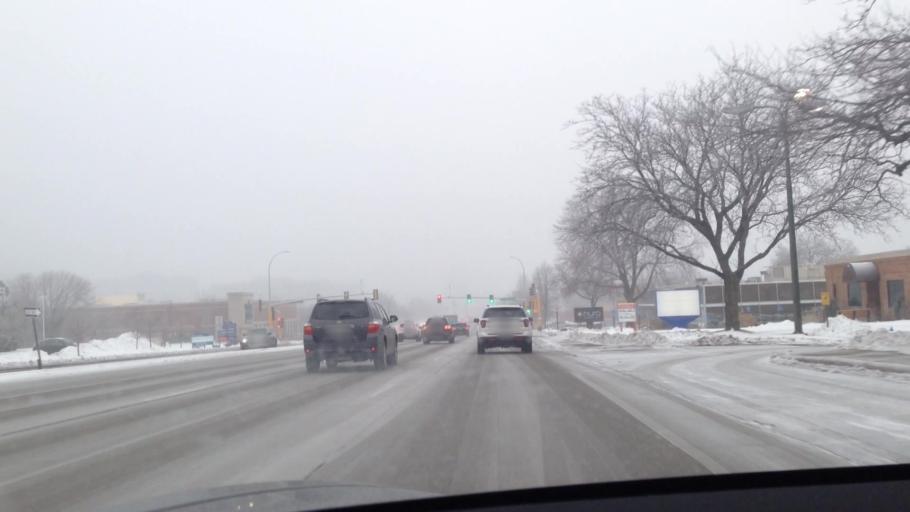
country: US
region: Minnesota
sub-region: Hennepin County
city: Edina
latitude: 44.8695
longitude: -93.3290
